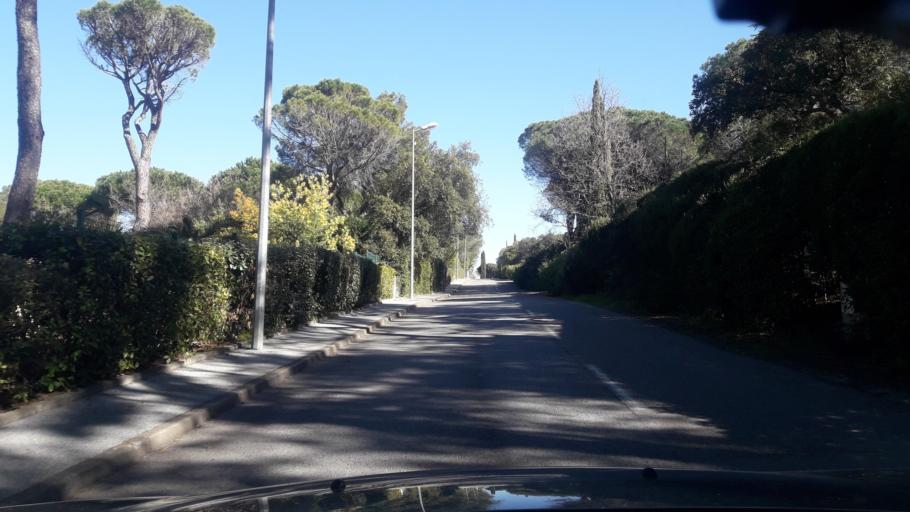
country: FR
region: Provence-Alpes-Cote d'Azur
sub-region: Departement du Var
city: Saint-Raphael
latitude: 43.4485
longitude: 6.7766
